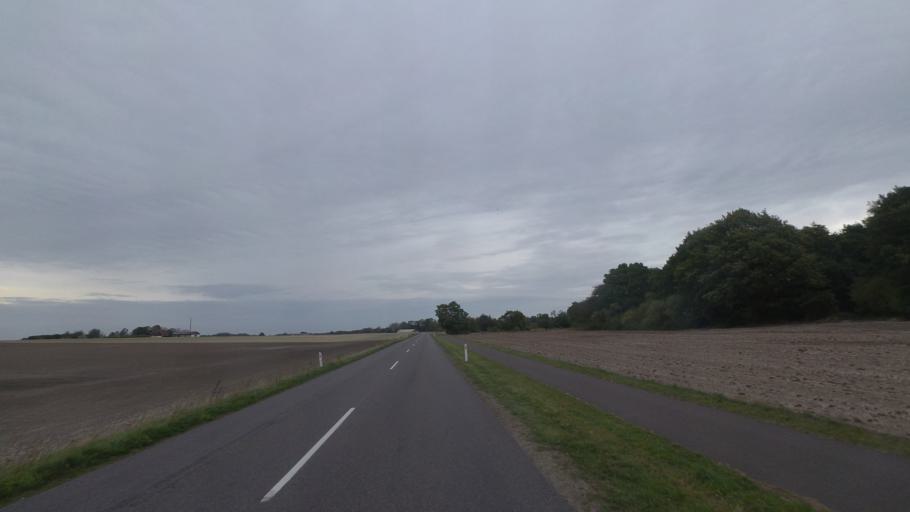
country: DK
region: Capital Region
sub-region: Bornholm Kommune
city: Nexo
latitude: 55.0034
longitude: 15.0822
